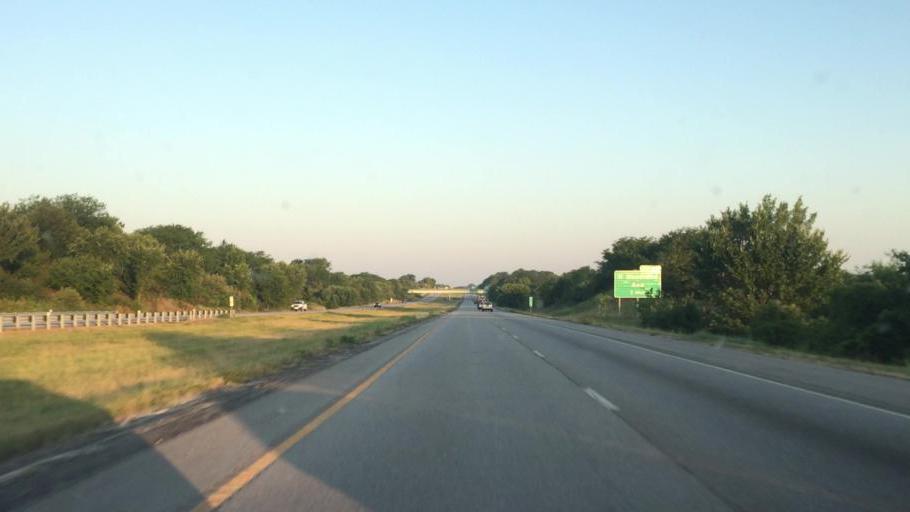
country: US
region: Missouri
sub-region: Clay County
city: Smithville
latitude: 39.3112
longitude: -94.5344
